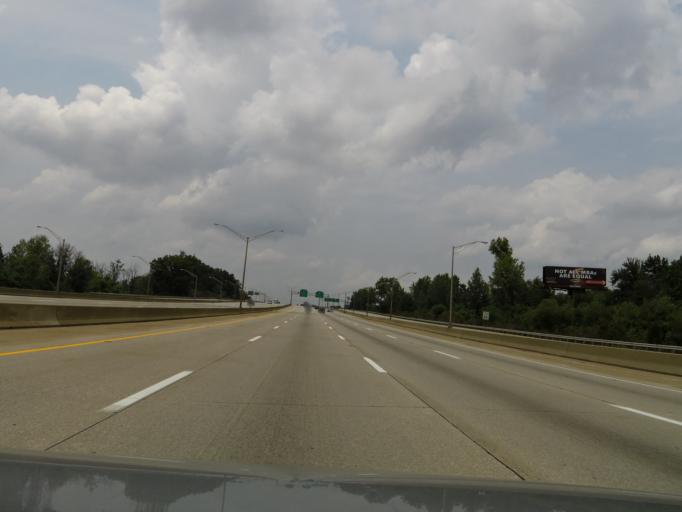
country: US
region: Kentucky
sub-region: Jefferson County
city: Heritage Creek
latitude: 38.1471
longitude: -85.7121
